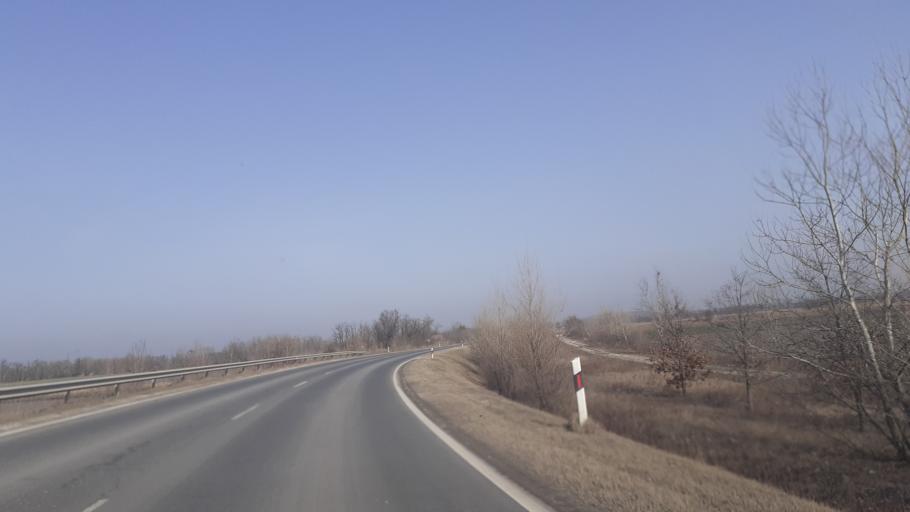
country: HU
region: Pest
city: Delegyhaza
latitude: 47.2324
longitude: 19.1161
